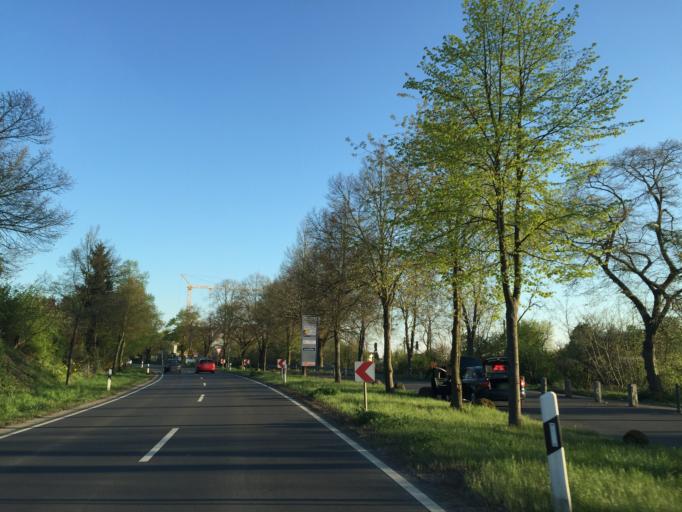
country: DE
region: Hesse
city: Zwingenberg
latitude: 49.7320
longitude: 8.6083
